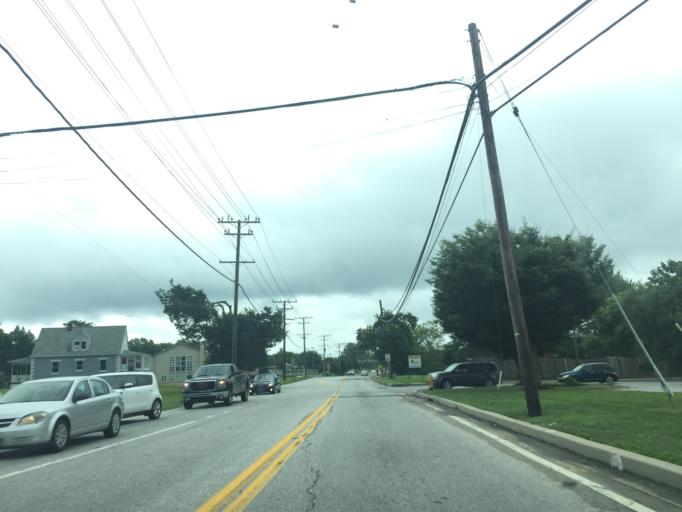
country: US
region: Maryland
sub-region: Harford County
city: Edgewood
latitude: 39.4481
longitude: -76.3006
